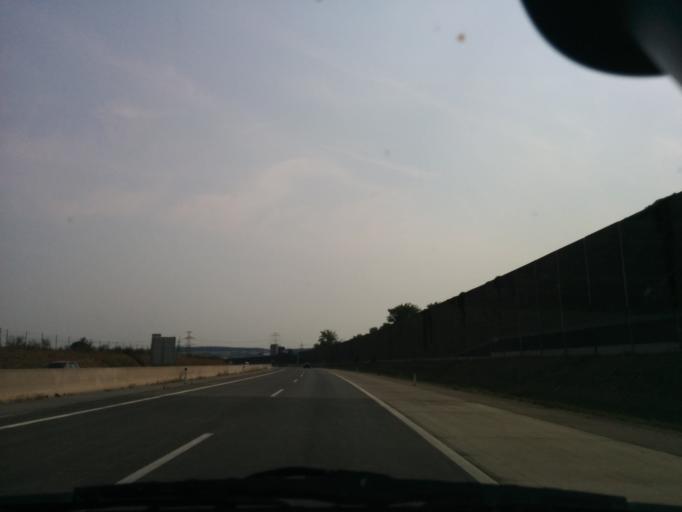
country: AT
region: Lower Austria
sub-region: Politischer Bezirk Korneuburg
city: Korneuburg
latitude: 48.3625
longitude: 16.3375
